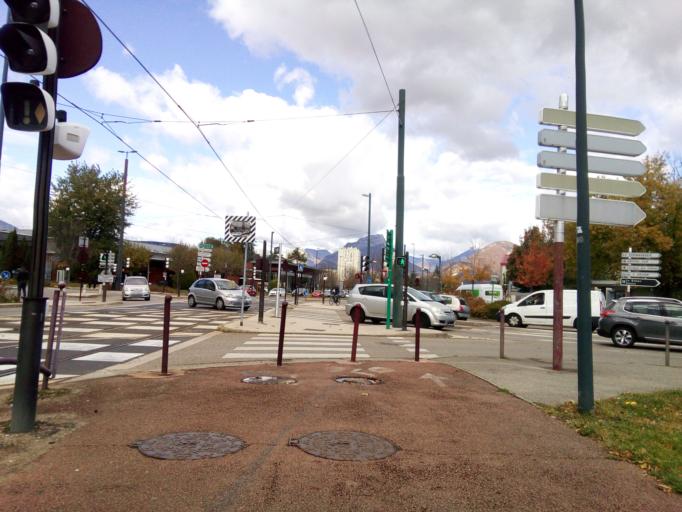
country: FR
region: Rhone-Alpes
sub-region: Departement de l'Isere
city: Echirolles
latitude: 45.1495
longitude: 5.7181
